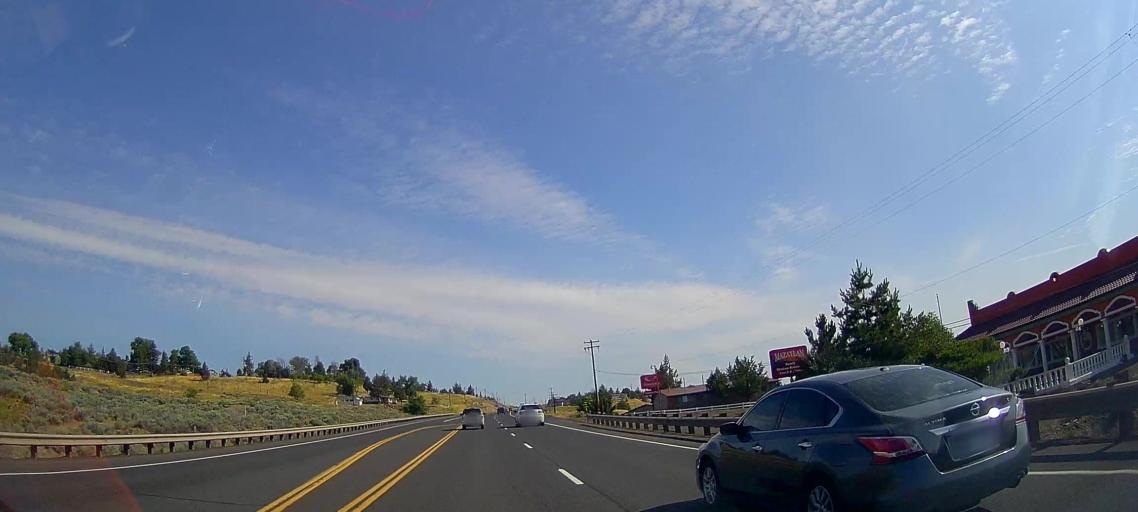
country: US
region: Oregon
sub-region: Jefferson County
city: Madras
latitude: 44.6448
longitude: -121.1295
